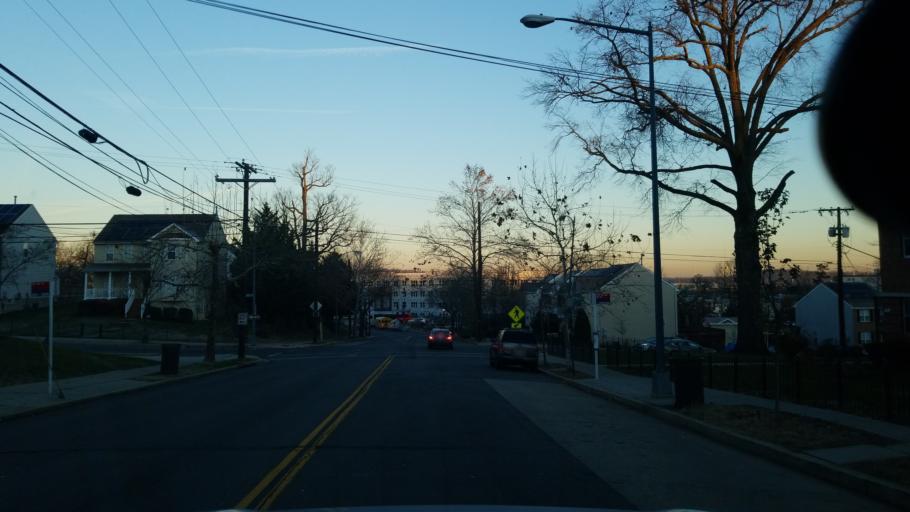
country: US
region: Maryland
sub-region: Prince George's County
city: Coral Hills
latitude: 38.8885
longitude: -76.9518
